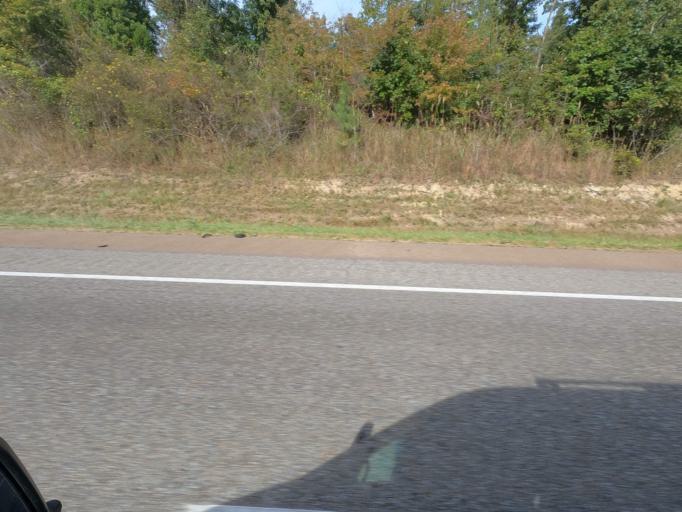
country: US
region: Tennessee
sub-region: Humphreys County
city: New Johnsonville
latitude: 35.8615
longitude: -88.0474
